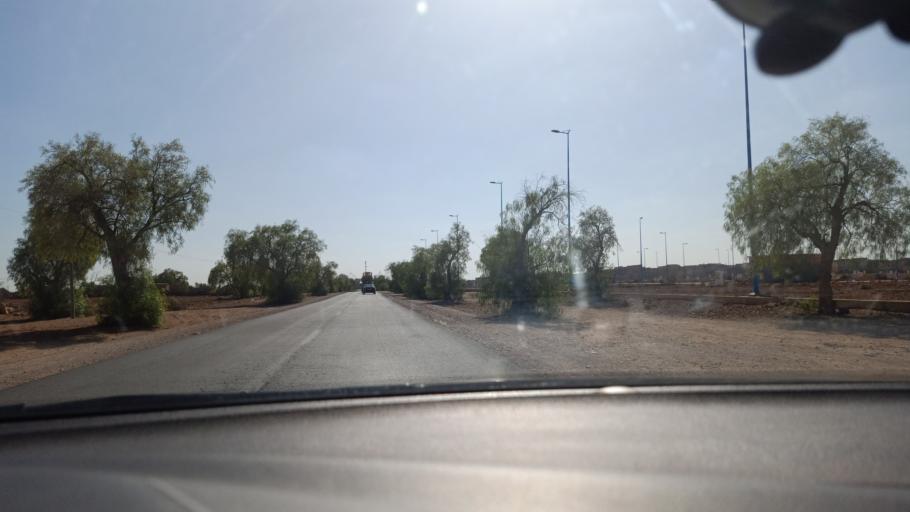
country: MA
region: Doukkala-Abda
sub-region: Safi
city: Youssoufia
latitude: 32.0900
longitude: -8.6175
